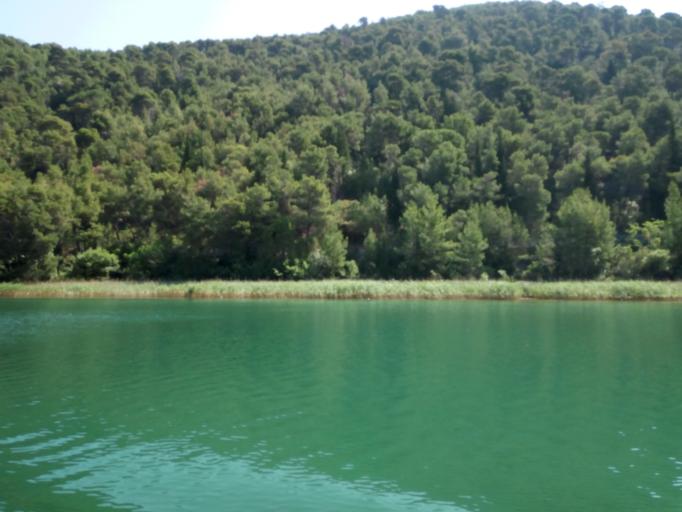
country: HR
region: Sibensko-Kniniska
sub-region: Grad Sibenik
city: Sibenik
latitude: 43.8183
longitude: 15.9491
